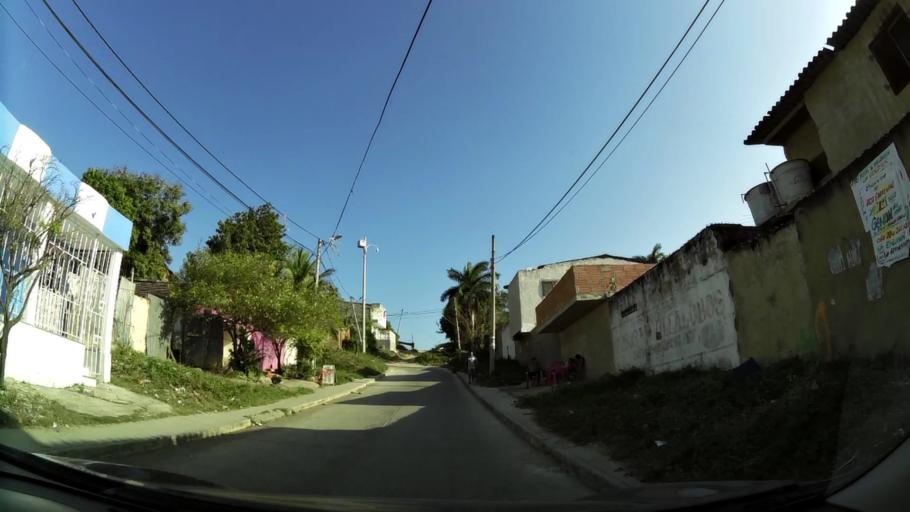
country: CO
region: Bolivar
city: Cartagena
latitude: 10.4034
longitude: -75.4808
